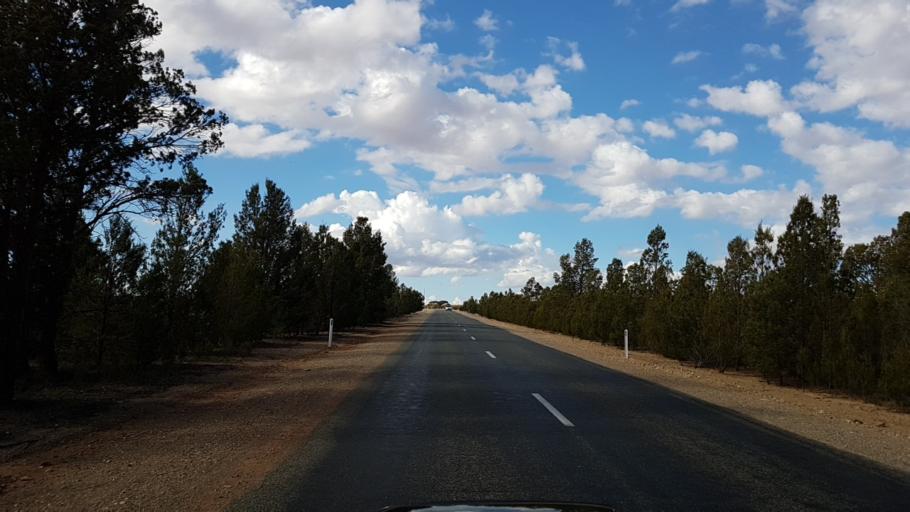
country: AU
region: South Australia
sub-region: Peterborough
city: Peterborough
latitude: -32.9625
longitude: 138.8857
